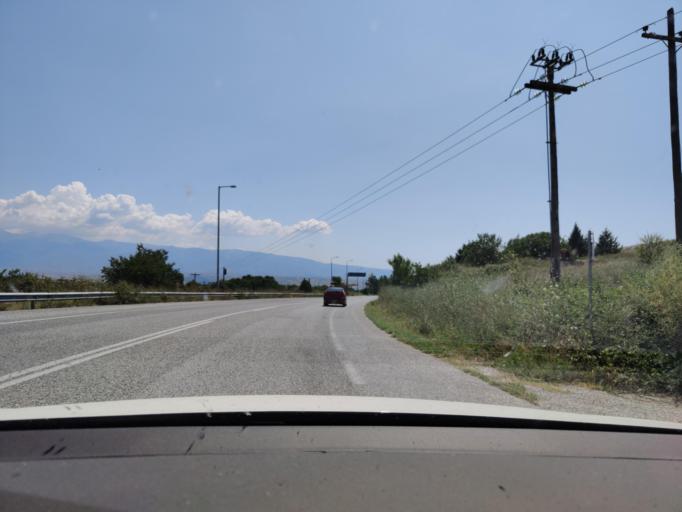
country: GR
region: Central Macedonia
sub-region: Nomos Serron
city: Nea Zichni
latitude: 41.0146
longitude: 23.8504
